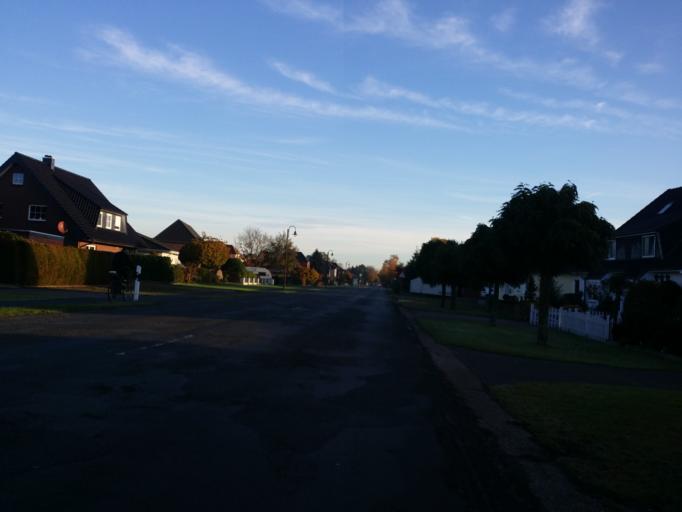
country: DE
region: Lower Saxony
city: Stuhr
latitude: 52.9988
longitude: 8.7712
